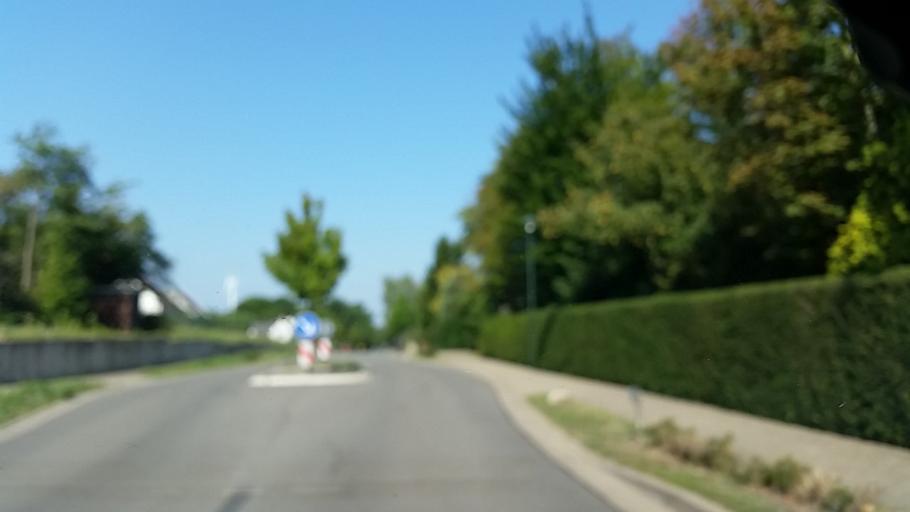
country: DE
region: Lower Saxony
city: Barwedel
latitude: 52.5243
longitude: 10.7722
